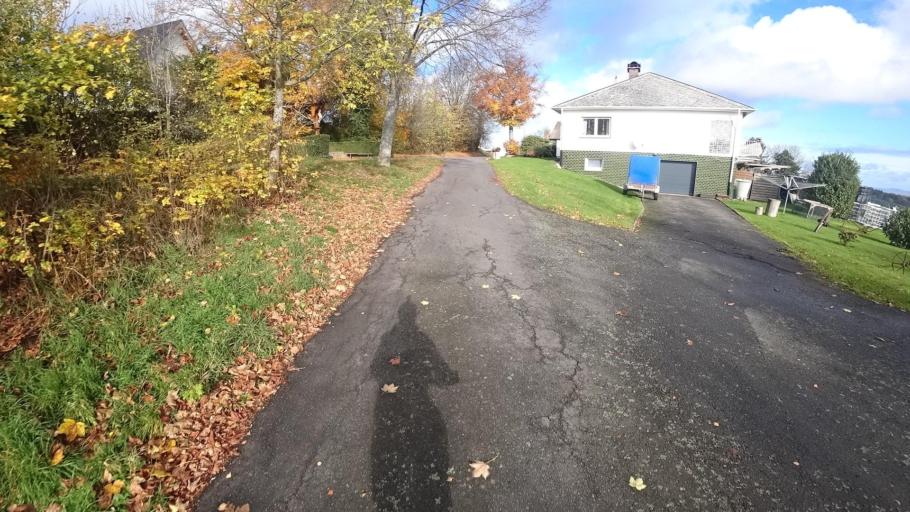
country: DE
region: Rheinland-Pfalz
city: Lind
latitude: 50.4924
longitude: 6.9376
